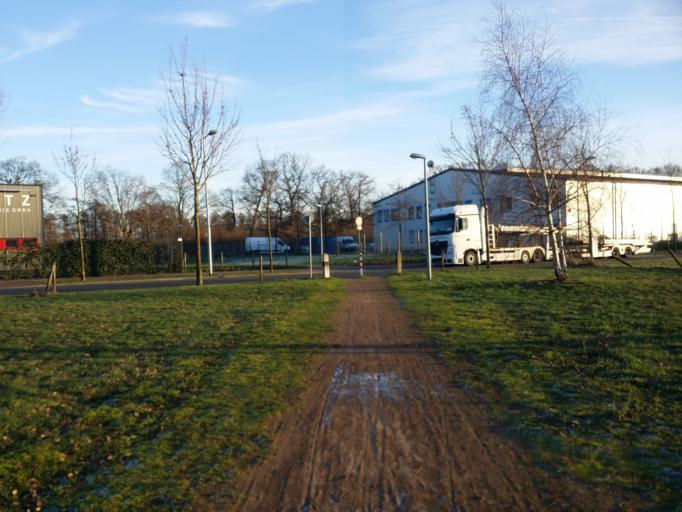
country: DE
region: Lower Saxony
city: Delmenhorst
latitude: 53.0447
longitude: 8.6780
